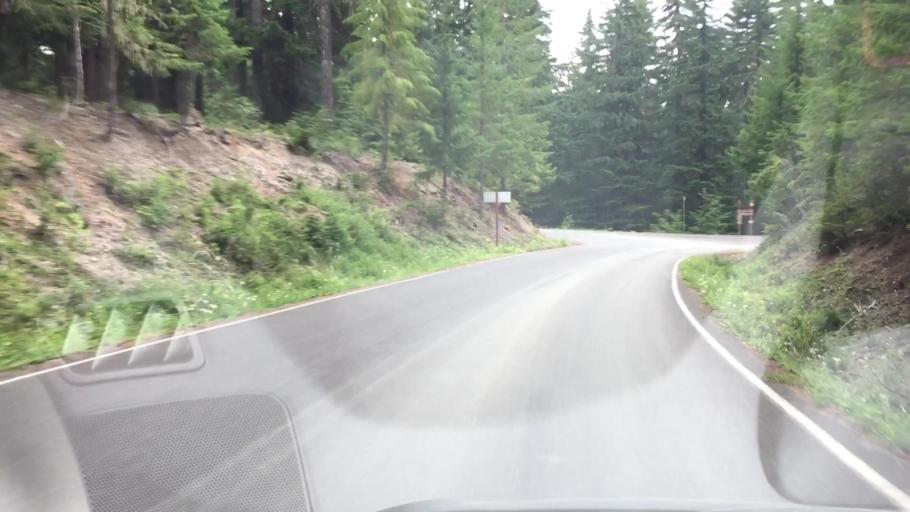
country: US
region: Washington
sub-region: Klickitat County
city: White Salmon
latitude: 46.2334
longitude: -121.6288
